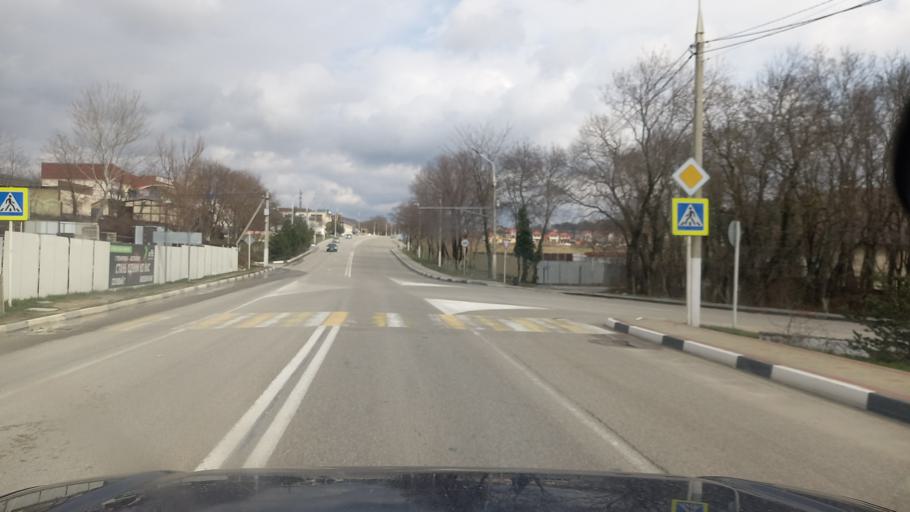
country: RU
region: Krasnodarskiy
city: Gelendzhik
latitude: 44.5545
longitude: 38.1113
